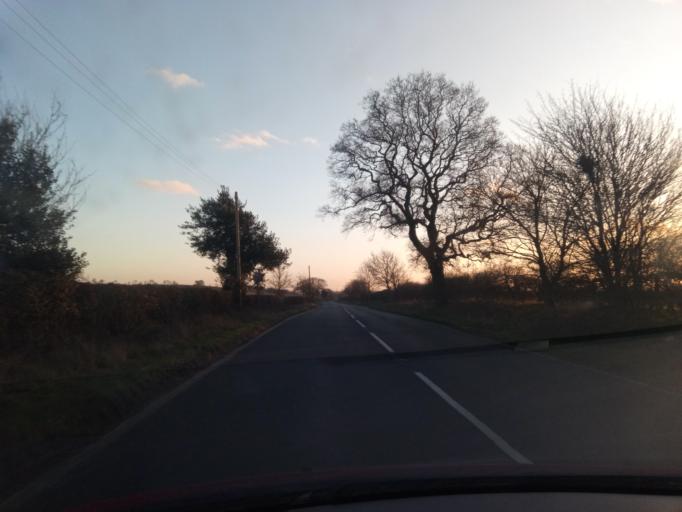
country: GB
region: England
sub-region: Nottinghamshire
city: Farnsfield
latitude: 53.0822
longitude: -1.0689
